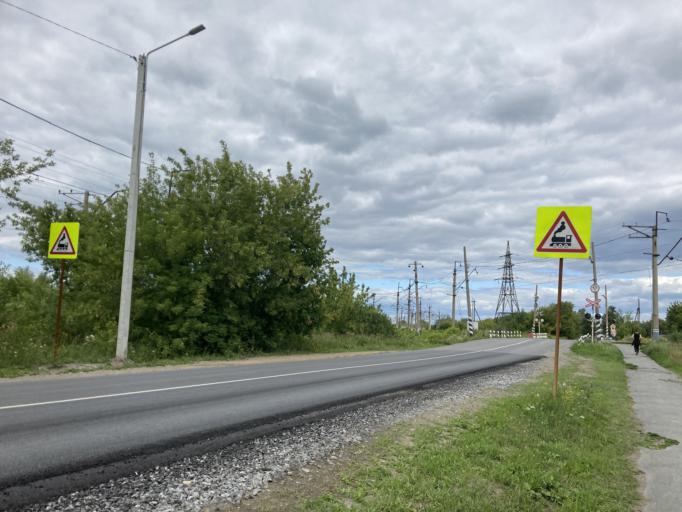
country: RU
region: Sverdlovsk
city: Bogdanovich
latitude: 56.7806
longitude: 62.0643
